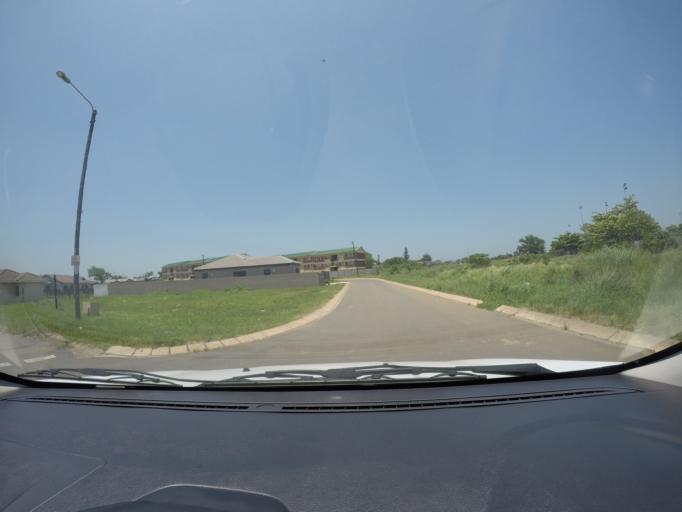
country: ZA
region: KwaZulu-Natal
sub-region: uThungulu District Municipality
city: eSikhawini
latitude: -28.8774
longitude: 31.8970
